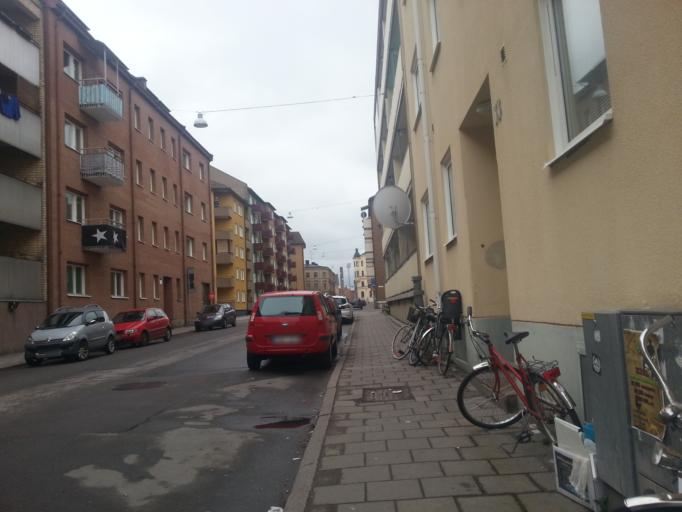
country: SE
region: OEstergoetland
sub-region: Norrkopings Kommun
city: Norrkoping
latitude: 58.5921
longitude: 16.1747
